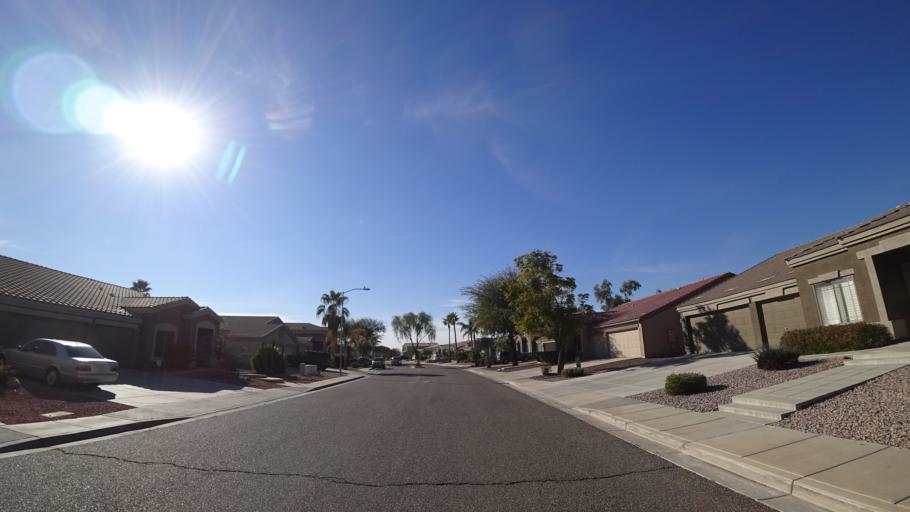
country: US
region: Arizona
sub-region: Maricopa County
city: Peoria
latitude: 33.5265
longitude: -112.2410
